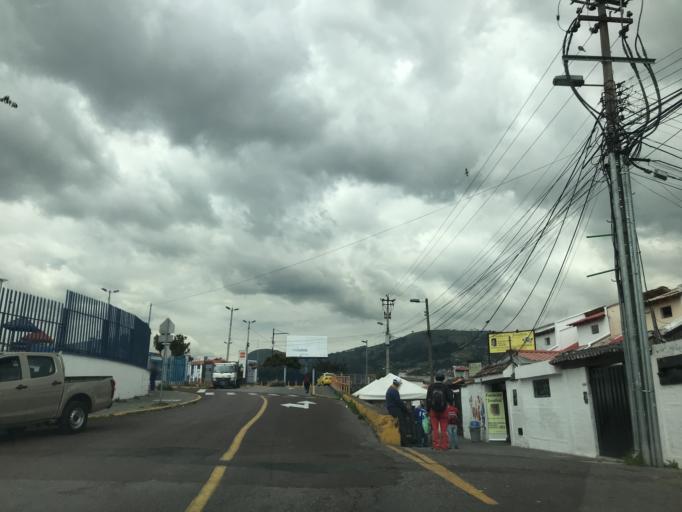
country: EC
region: Pichincha
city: Quito
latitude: -0.2189
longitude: -78.4987
